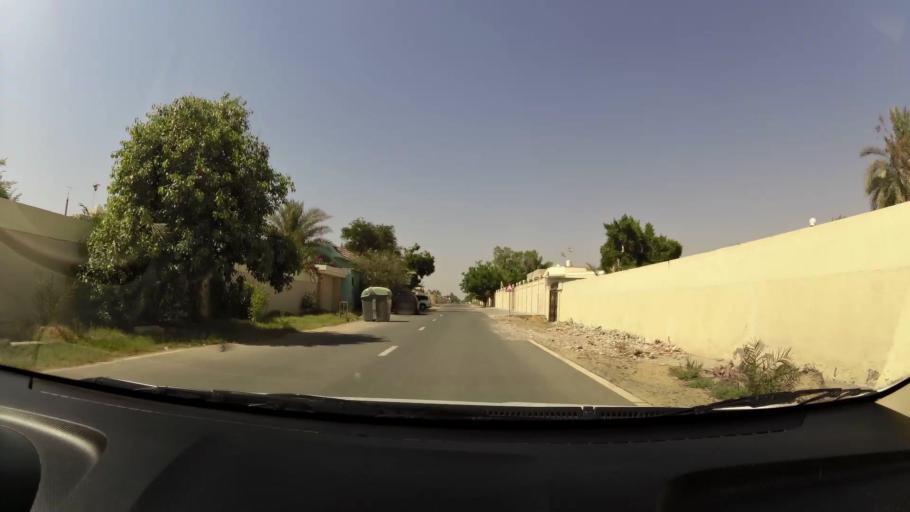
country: AE
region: Ajman
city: Ajman
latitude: 25.4053
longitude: 55.4758
